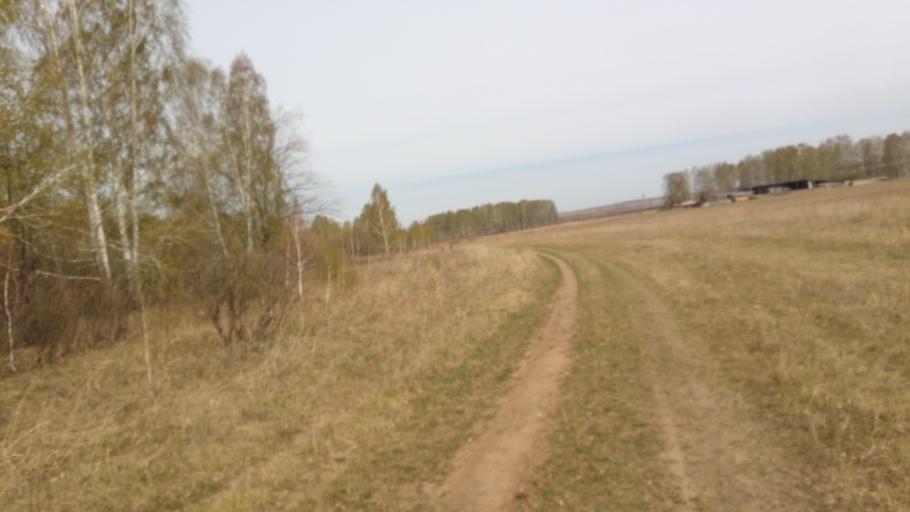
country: RU
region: Chelyabinsk
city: Timiryazevskiy
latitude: 55.0236
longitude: 60.8598
